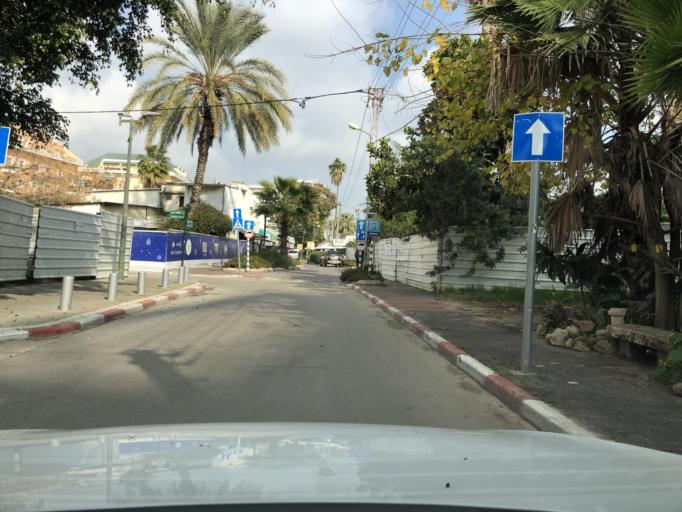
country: IL
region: Central District
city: Yehud
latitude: 32.0292
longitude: 34.8890
